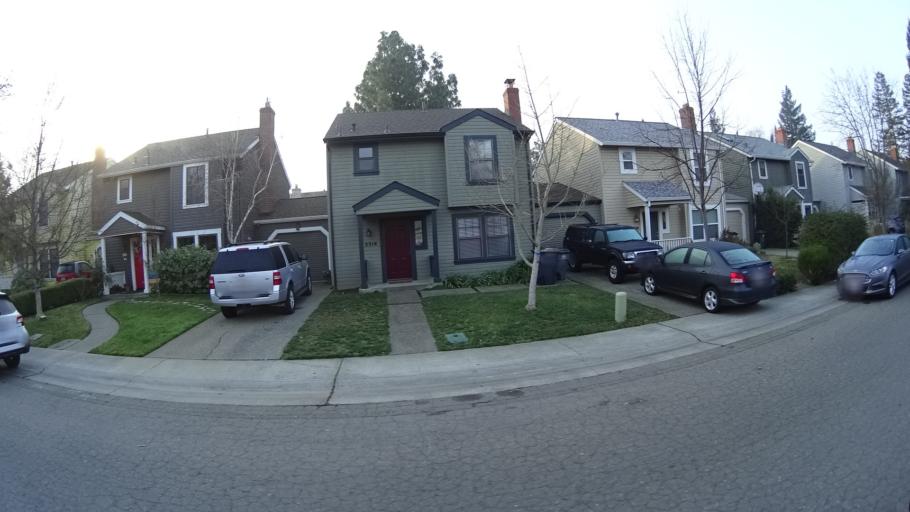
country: US
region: California
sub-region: Yolo County
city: Davis
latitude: 38.5638
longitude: -121.7449
